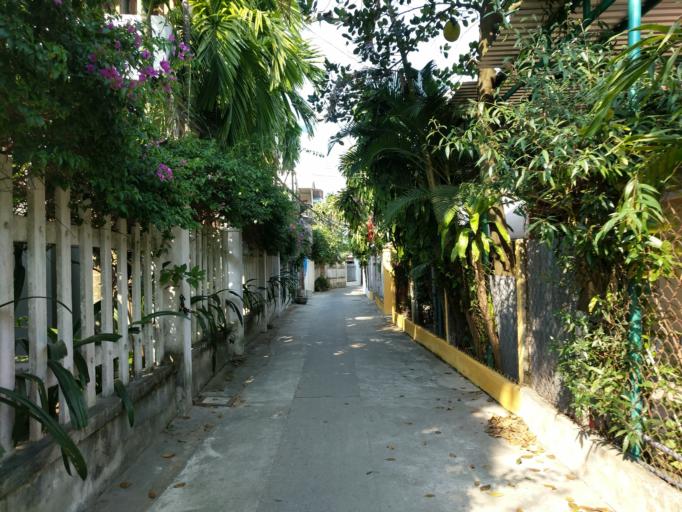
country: VN
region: Quang Nam
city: Hoi An
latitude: 15.8830
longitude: 108.3257
